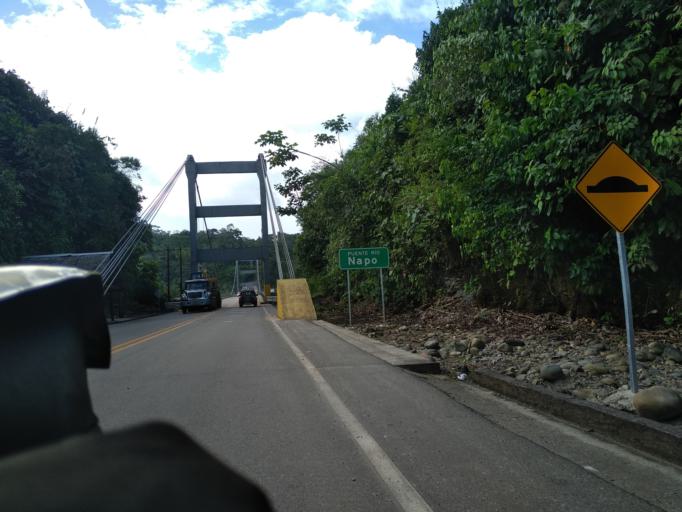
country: EC
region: Napo
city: Tena
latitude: -1.0463
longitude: -77.7965
